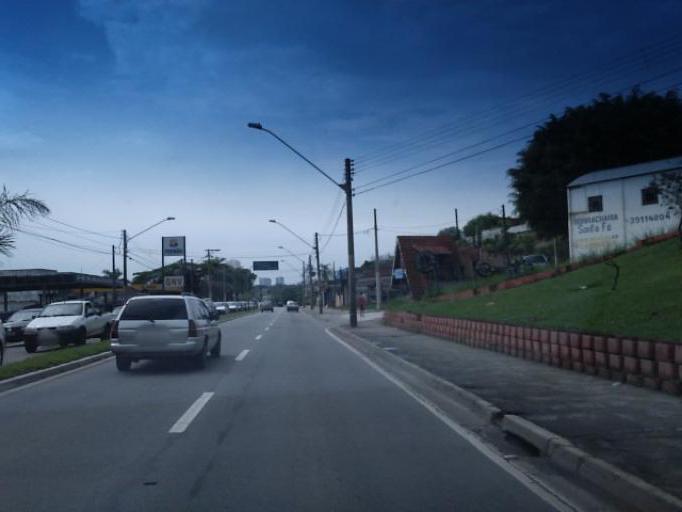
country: BR
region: Sao Paulo
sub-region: Sao Jose Dos Campos
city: Sao Jose dos Campos
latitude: -23.1744
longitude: -45.8783
